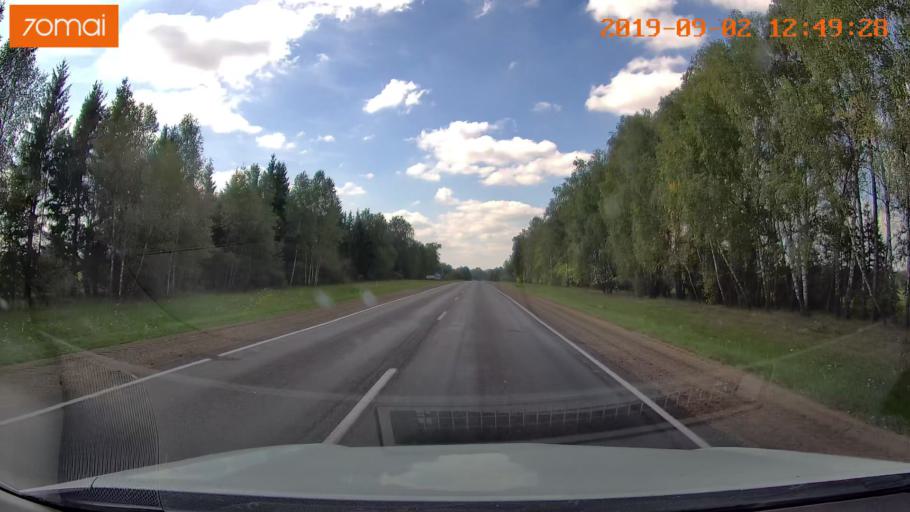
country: BY
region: Mogilev
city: Klimavichy
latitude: 53.7363
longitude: 32.1676
